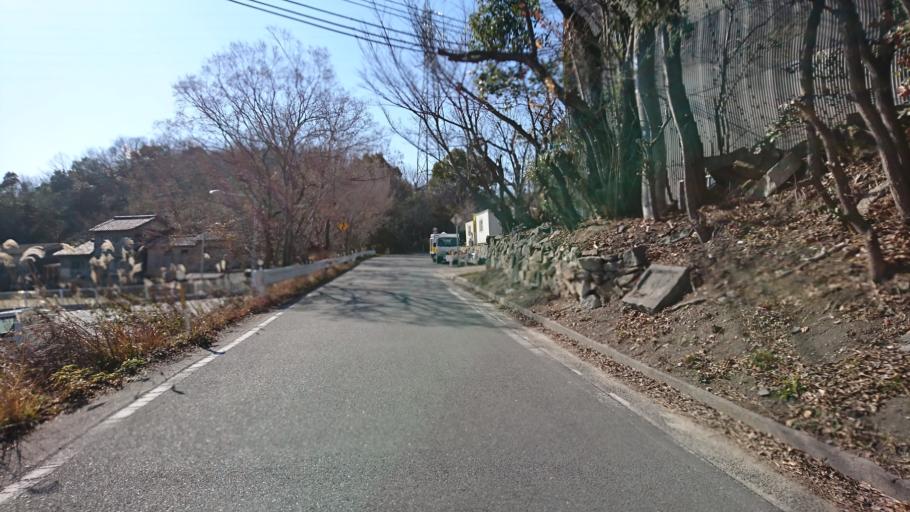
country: JP
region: Hyogo
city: Kakogawacho-honmachi
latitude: 34.7886
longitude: 134.7966
